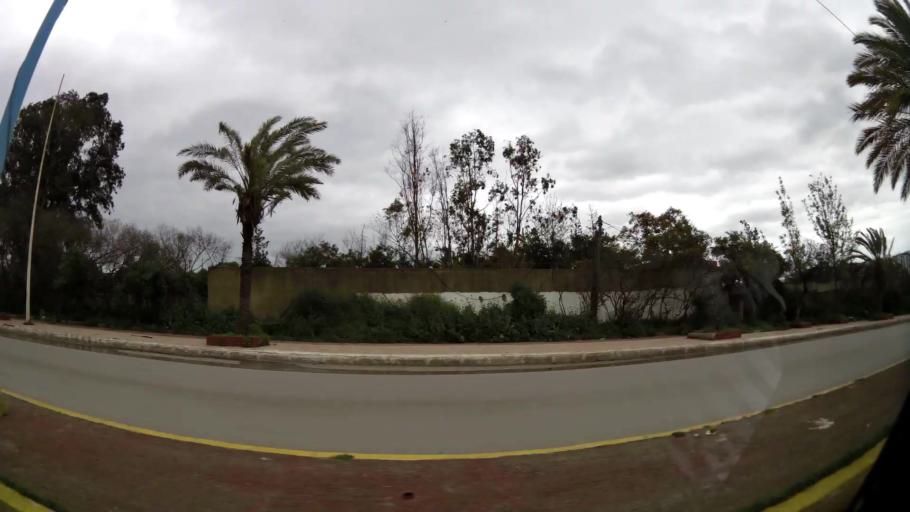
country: MA
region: Grand Casablanca
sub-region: Mediouna
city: Tit Mellil
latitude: 33.5582
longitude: -7.5382
